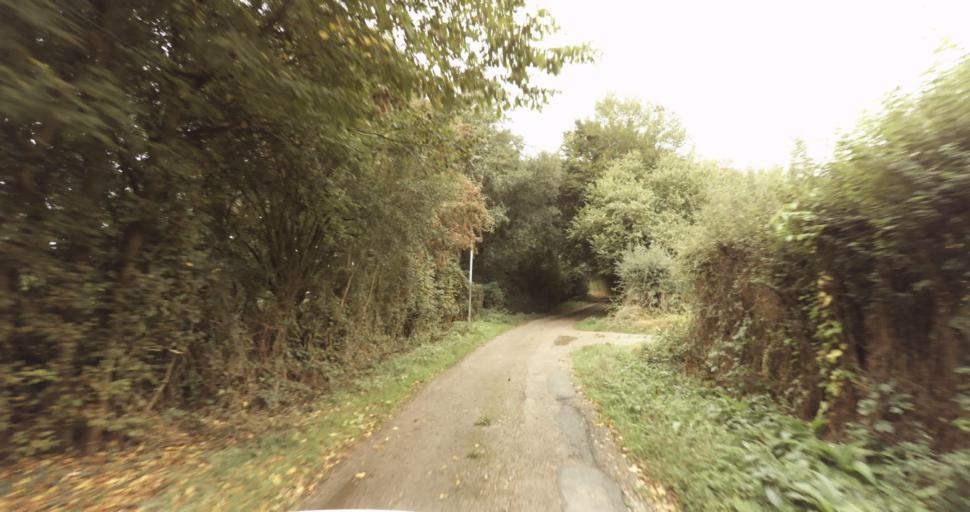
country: FR
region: Lower Normandy
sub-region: Departement du Calvados
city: Livarot
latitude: 48.9285
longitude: 0.0922
